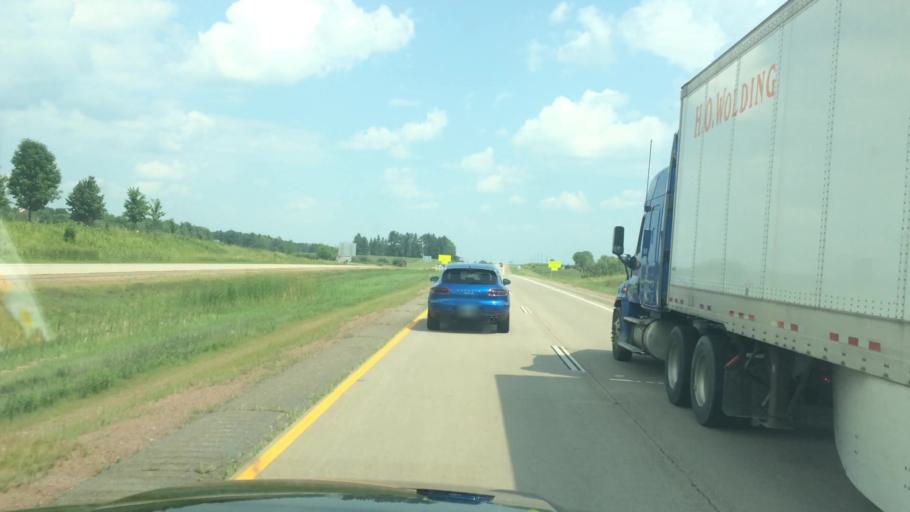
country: US
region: Wisconsin
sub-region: Clark County
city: Abbotsford
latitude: 44.9458
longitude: -90.2727
